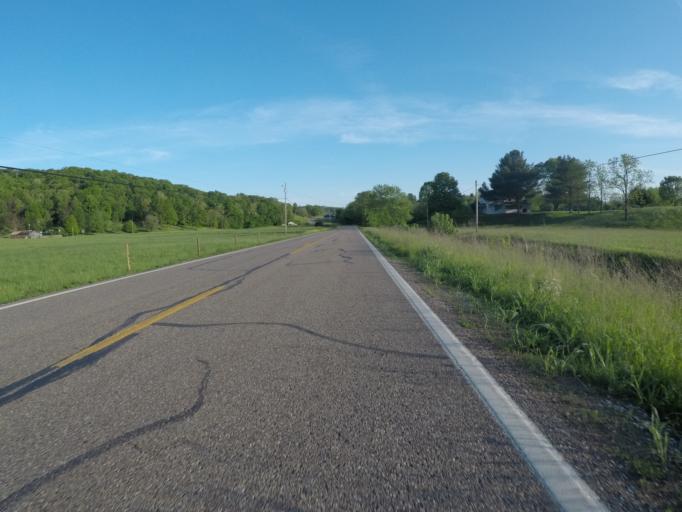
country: US
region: West Virginia
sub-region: Cabell County
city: Huntington
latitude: 38.5381
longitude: -82.4607
